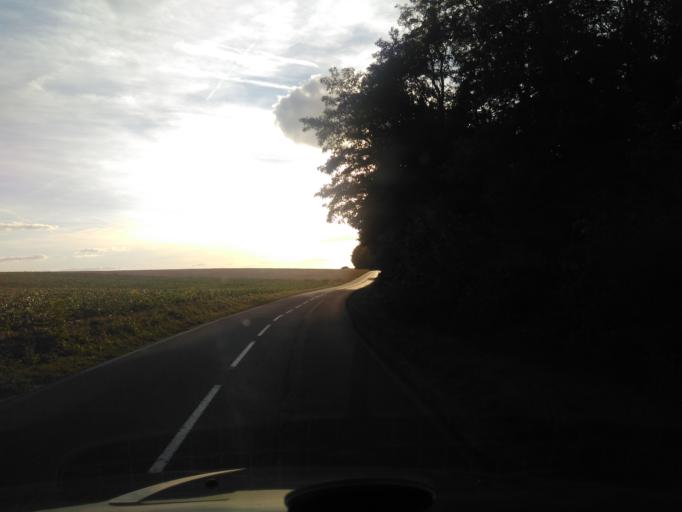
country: FR
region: Picardie
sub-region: Departement de l'Aisne
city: Saint-Erme-Outre-et-Ramecourt
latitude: 49.4395
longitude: 3.7609
